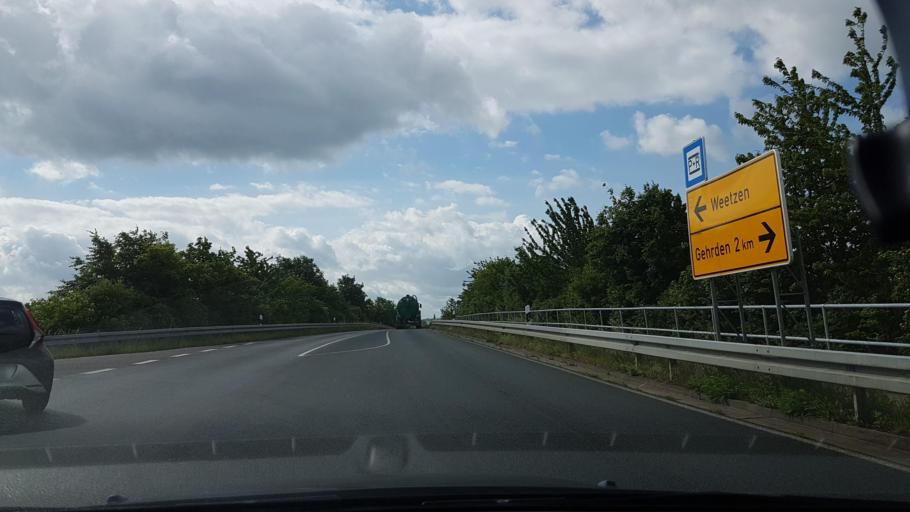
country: DE
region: Lower Saxony
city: Ronnenberg
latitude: 52.3058
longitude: 9.6342
